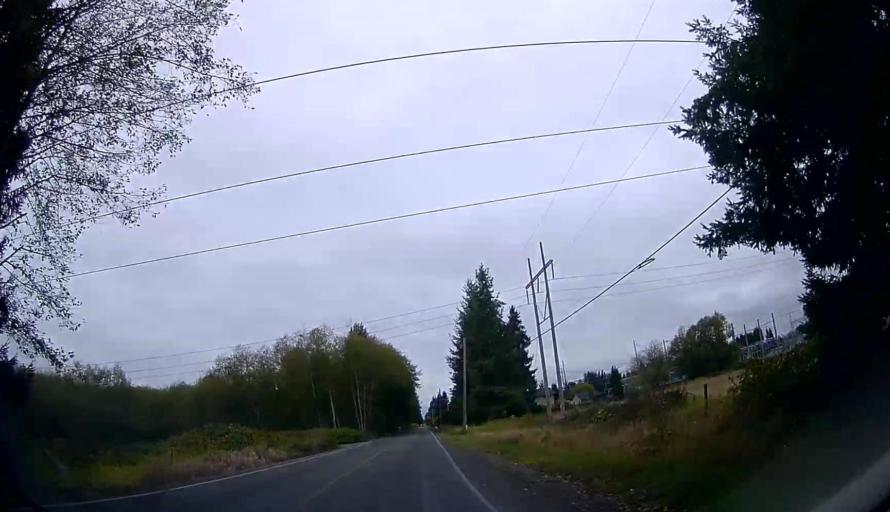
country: US
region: Washington
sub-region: Skagit County
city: Sedro-Woolley
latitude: 48.5032
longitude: -122.2005
